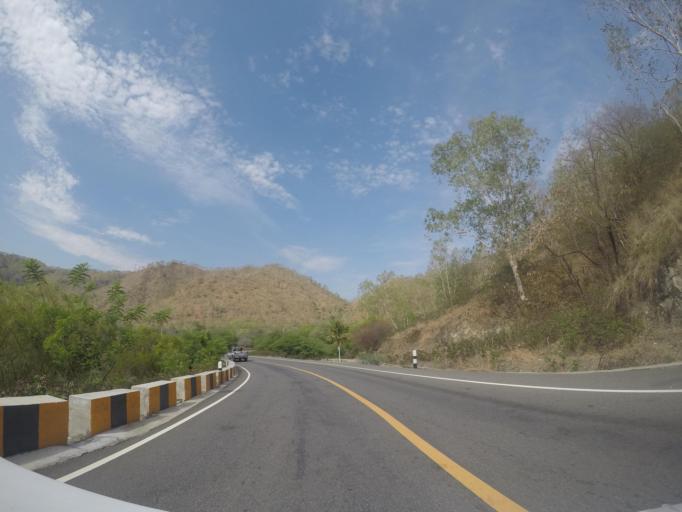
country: ID
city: Metinaro
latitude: -8.5249
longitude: 125.7204
